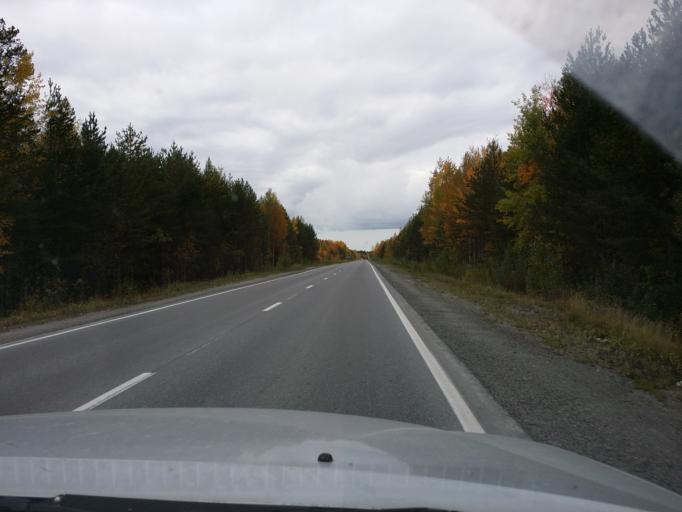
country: RU
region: Khanty-Mansiyskiy Avtonomnyy Okrug
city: Langepas
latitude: 61.2027
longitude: 75.3985
